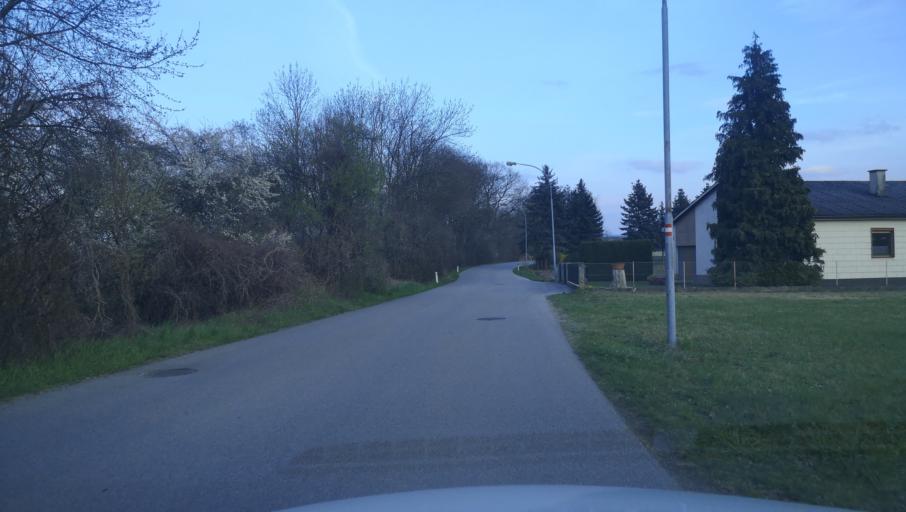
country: AT
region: Lower Austria
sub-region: Politischer Bezirk Amstetten
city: Amstetten
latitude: 48.1115
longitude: 14.8848
